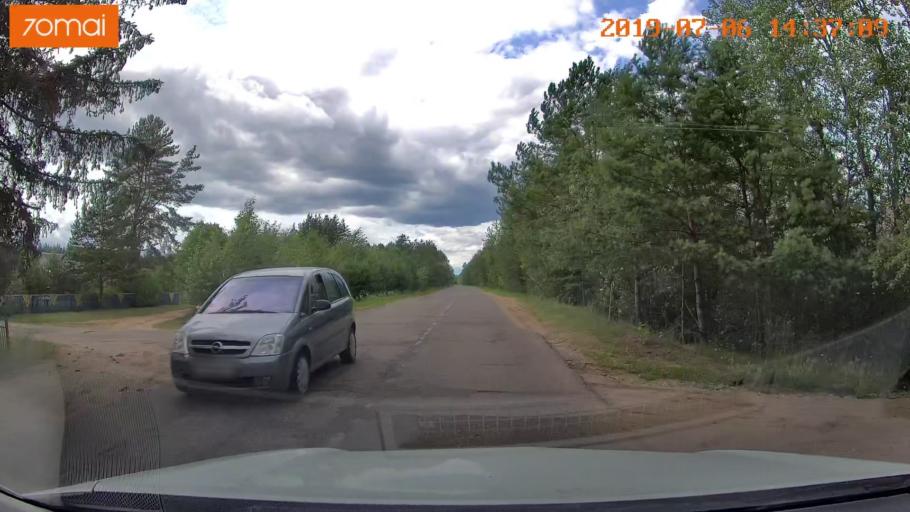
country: BY
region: Minsk
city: Ivyanyets
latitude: 53.8948
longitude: 26.7239
